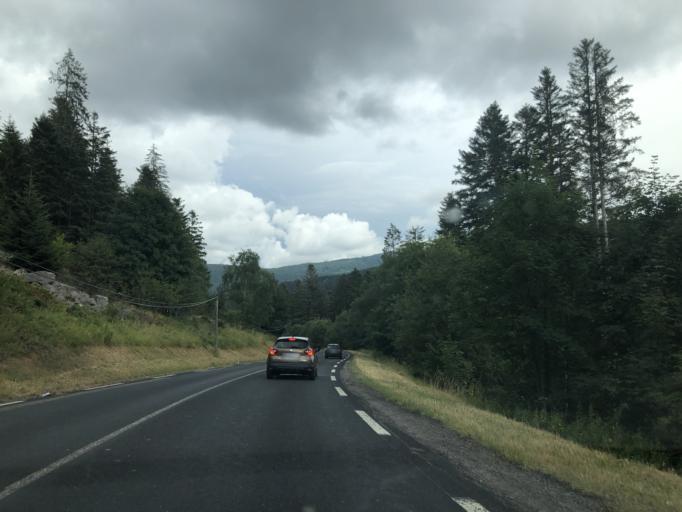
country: FR
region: Lorraine
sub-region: Departement des Vosges
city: Xonrupt-Longemer
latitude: 48.0874
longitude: 6.9049
